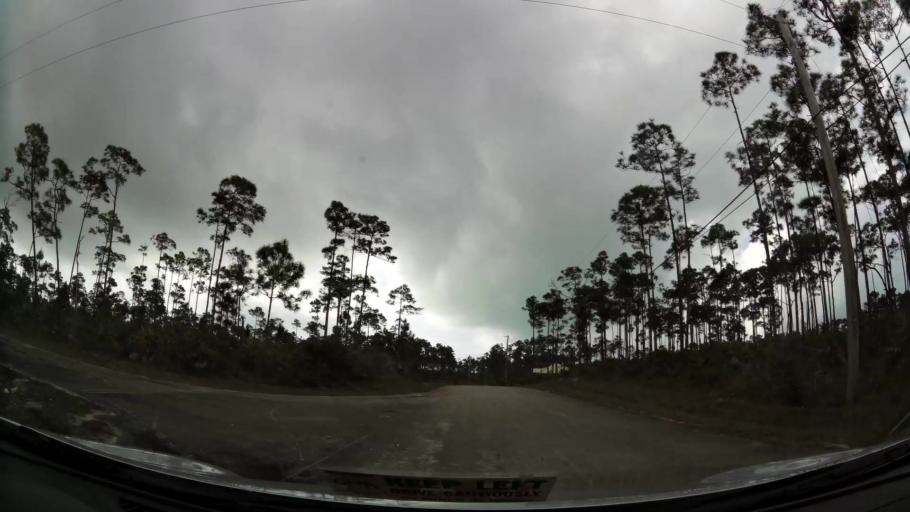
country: BS
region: Freeport
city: Lucaya
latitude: 26.5577
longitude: -78.5790
